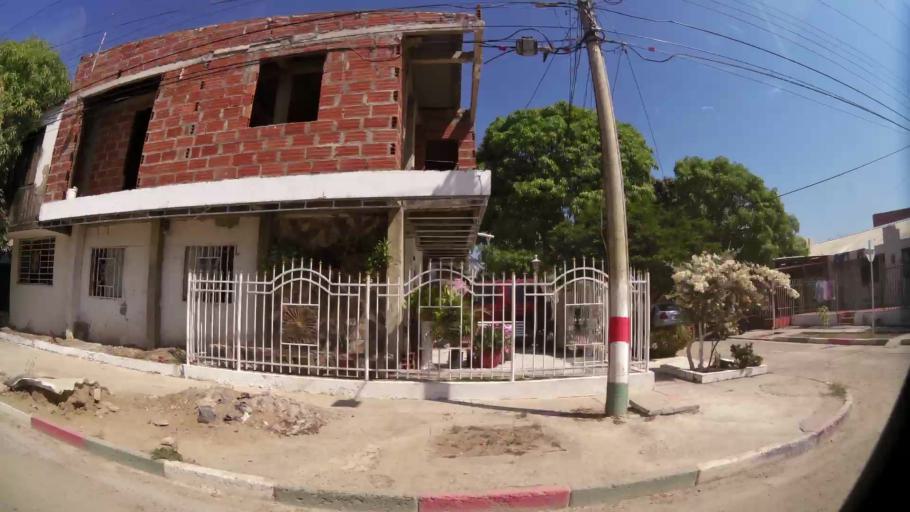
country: CO
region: Bolivar
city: Cartagena
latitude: 10.3851
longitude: -75.4528
